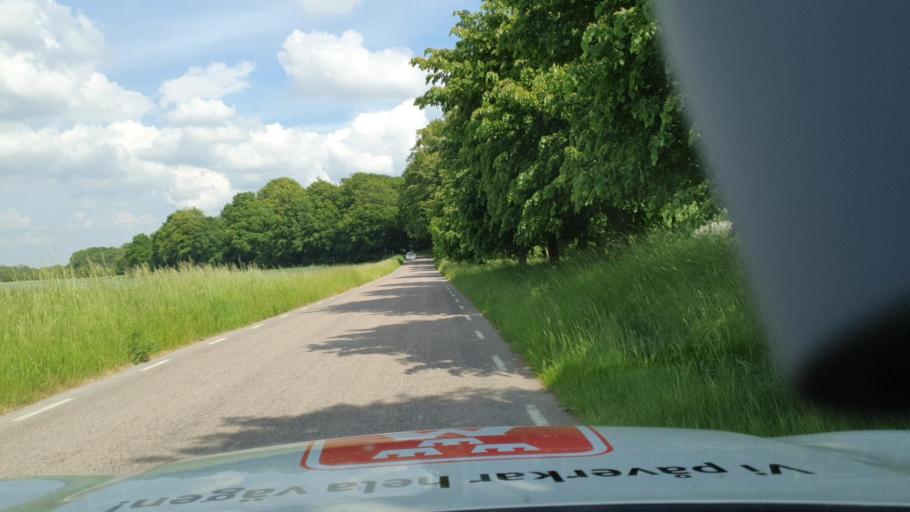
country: SE
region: Skane
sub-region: Svedala Kommun
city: Svedala
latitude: 55.5339
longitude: 13.2181
